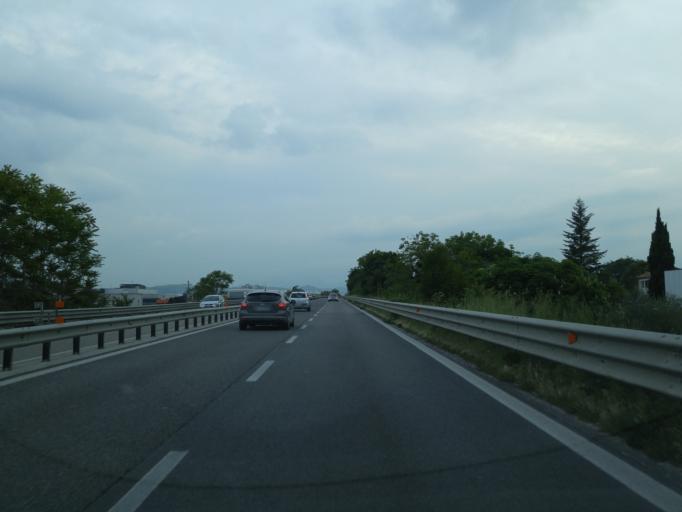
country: IT
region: The Marches
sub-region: Provincia di Pesaro e Urbino
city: Bellocchi
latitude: 43.7966
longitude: 13.0054
